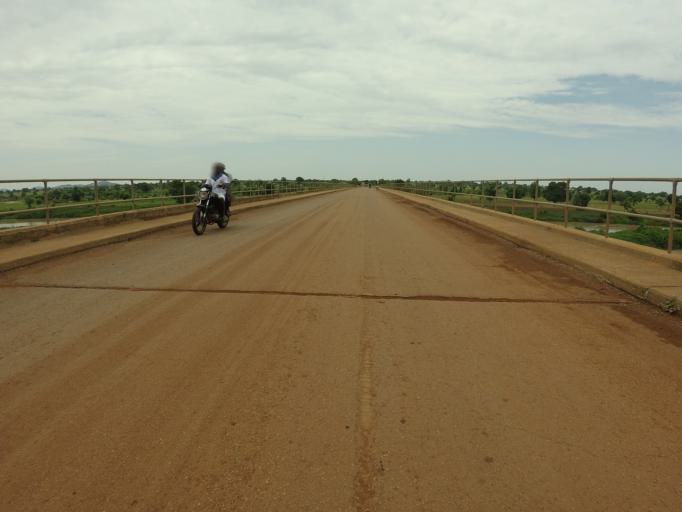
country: GH
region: Upper East
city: Bawku
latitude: 11.0026
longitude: -0.3850
